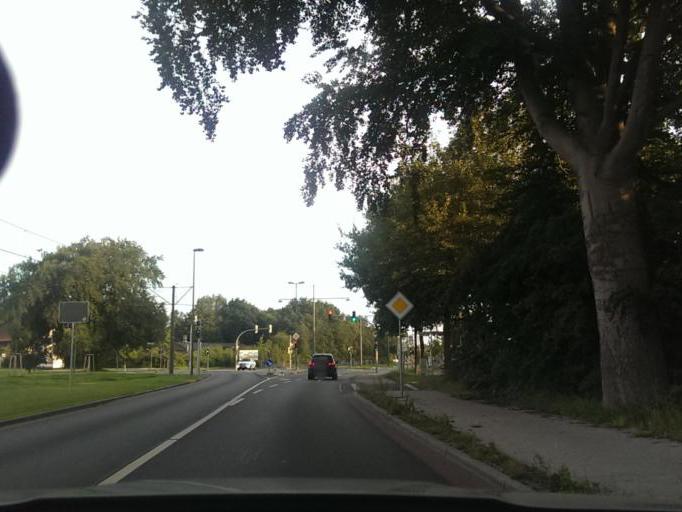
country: DE
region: Lower Saxony
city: Lilienthal
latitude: 53.1305
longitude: 8.8988
